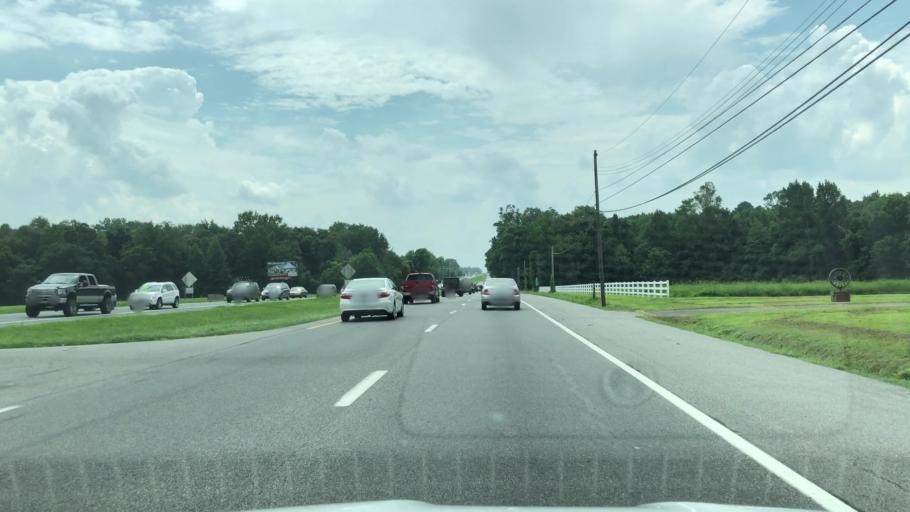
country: US
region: Delaware
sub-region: Kent County
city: Woodside East
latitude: 39.0401
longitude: -75.5593
